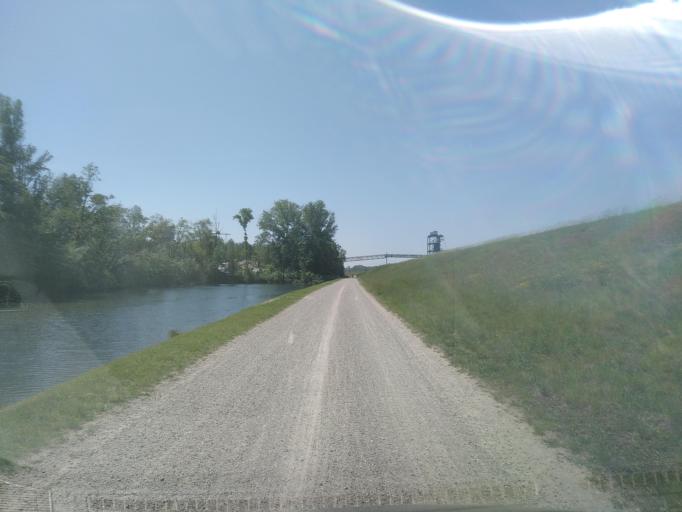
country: FR
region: Alsace
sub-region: Departement du Haut-Rhin
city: Kunheim
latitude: 48.0931
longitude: 7.5775
